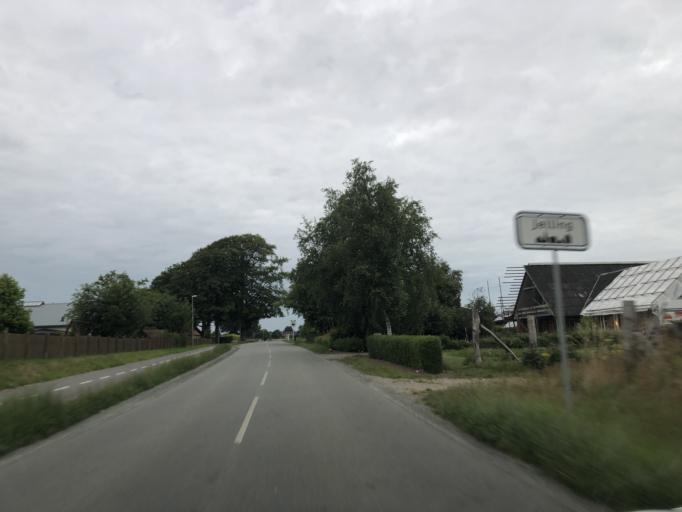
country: DK
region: South Denmark
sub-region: Vejle Kommune
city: Jelling
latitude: 55.7436
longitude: 9.4140
